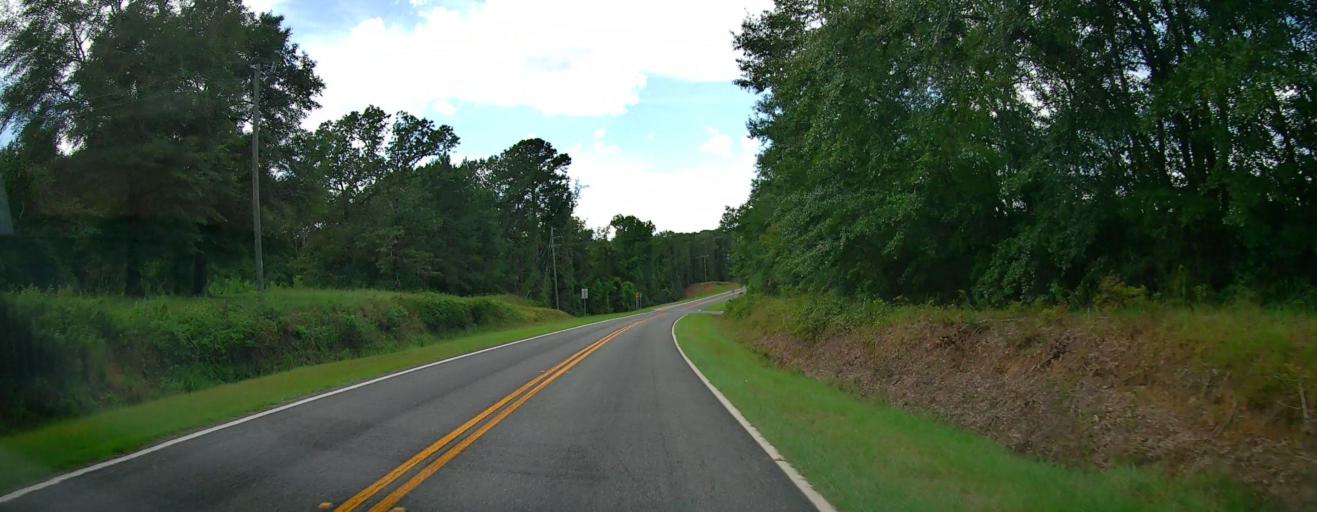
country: US
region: Georgia
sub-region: Taylor County
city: Butler
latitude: 32.4367
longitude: -84.1943
